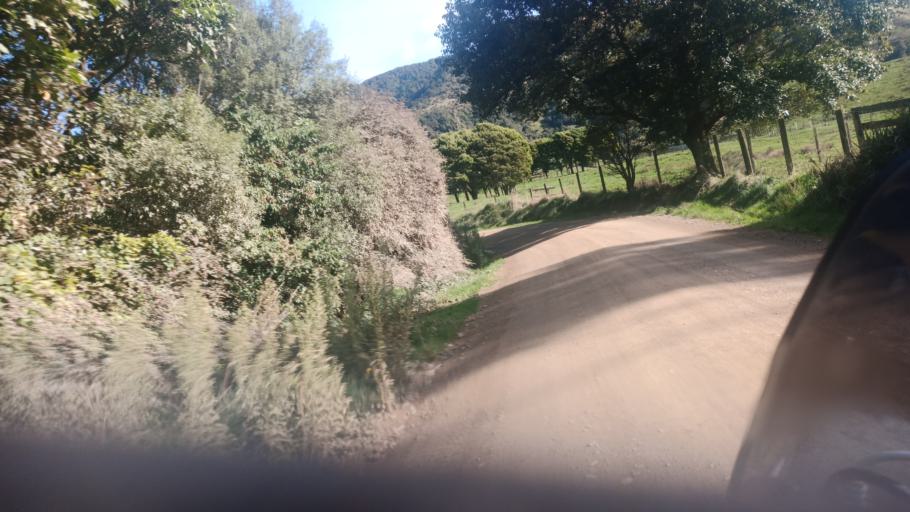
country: NZ
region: Bay of Plenty
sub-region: Opotiki District
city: Opotiki
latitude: -38.4356
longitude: 177.5472
